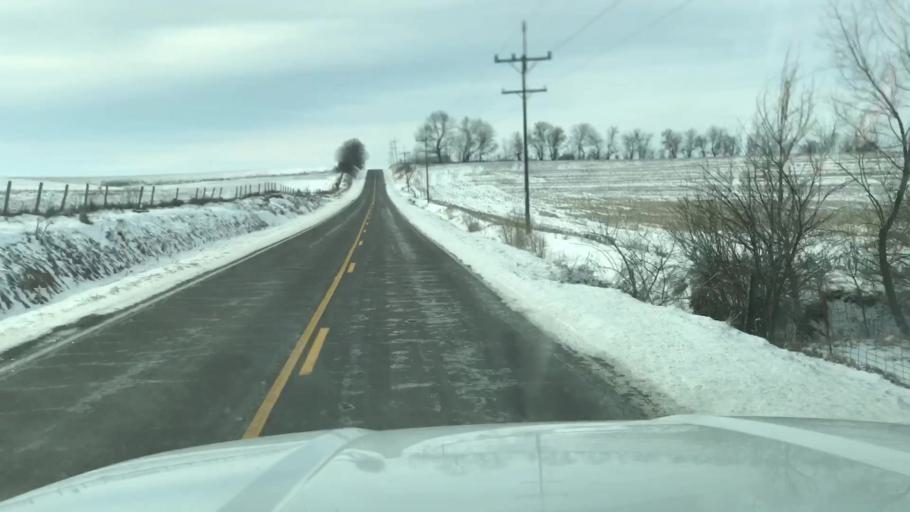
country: US
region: Missouri
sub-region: Holt County
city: Oregon
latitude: 40.0749
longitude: -95.1355
